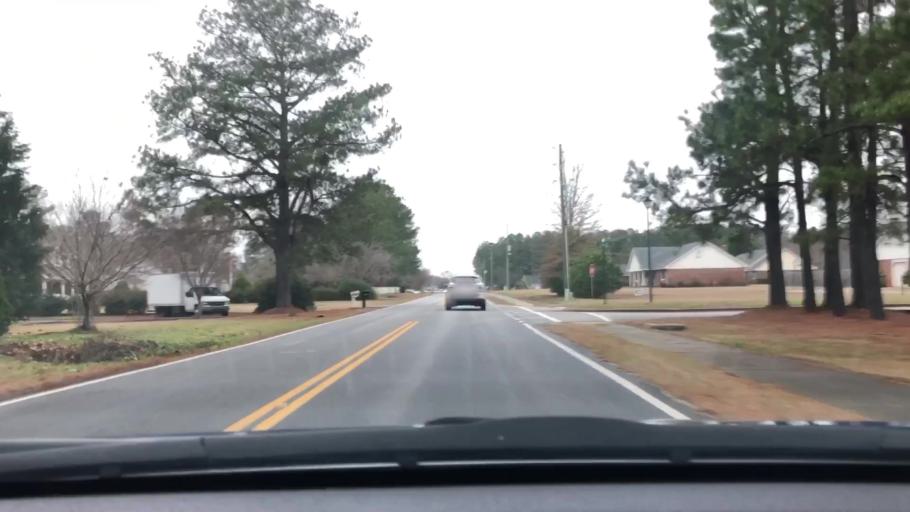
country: US
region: South Carolina
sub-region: Sumter County
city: Cherryvale
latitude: 33.9364
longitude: -80.4139
